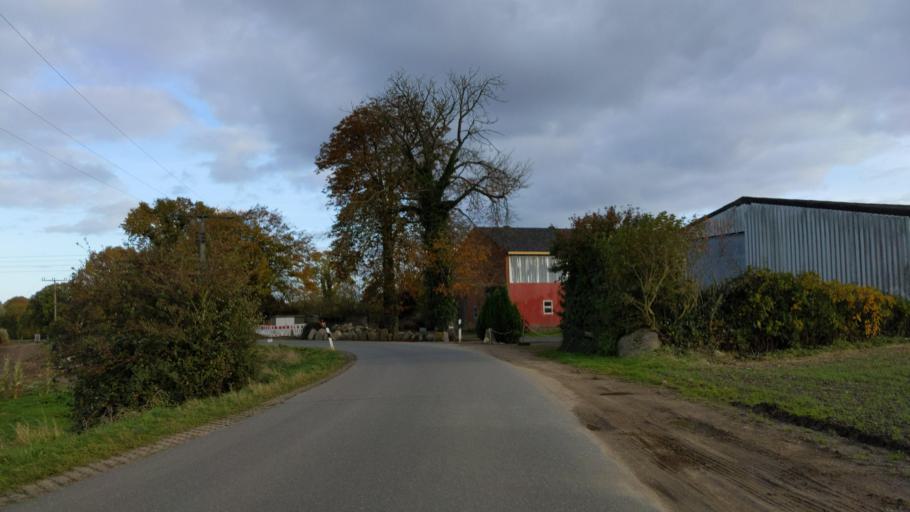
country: DE
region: Schleswig-Holstein
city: Susel
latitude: 54.1017
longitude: 10.7257
